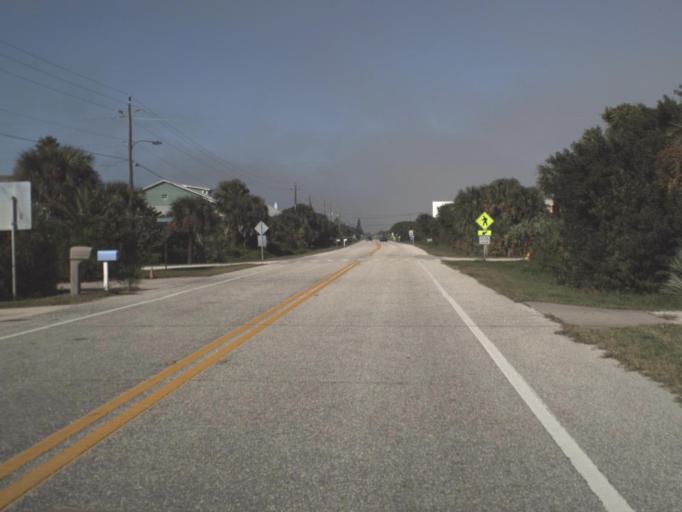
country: US
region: Florida
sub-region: Volusia County
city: Edgewater
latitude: 28.9441
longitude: -80.8354
